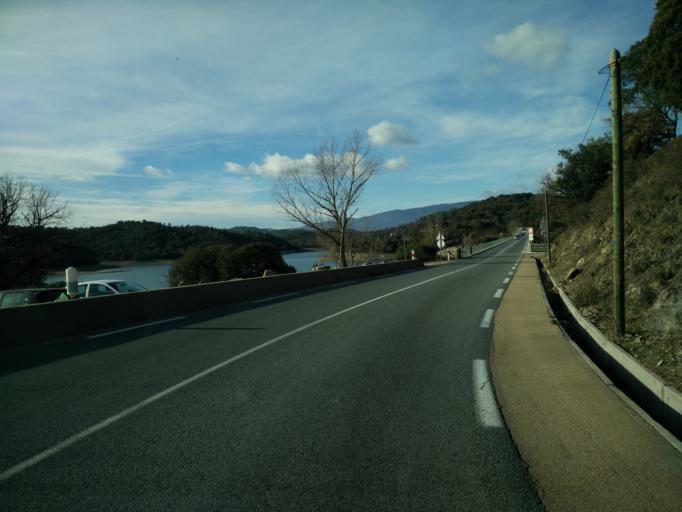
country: FR
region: Provence-Alpes-Cote d'Azur
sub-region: Departement du Var
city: Montauroux
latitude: 43.5818
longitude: 6.8052
